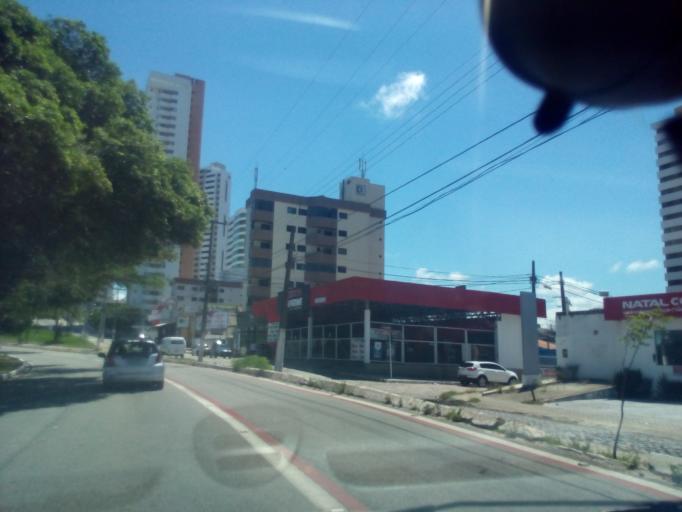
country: BR
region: Rio Grande do Norte
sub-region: Natal
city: Natal
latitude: -5.8280
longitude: -35.2175
